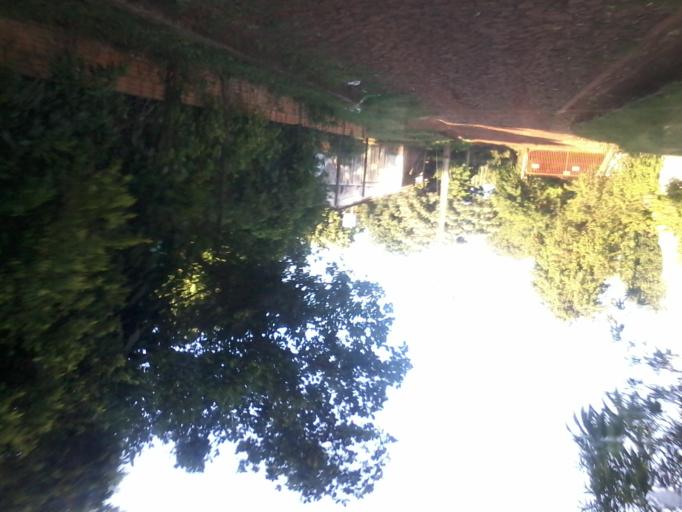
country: PY
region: Alto Parana
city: Ciudad del Este
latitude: -25.4375
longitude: -54.6443
